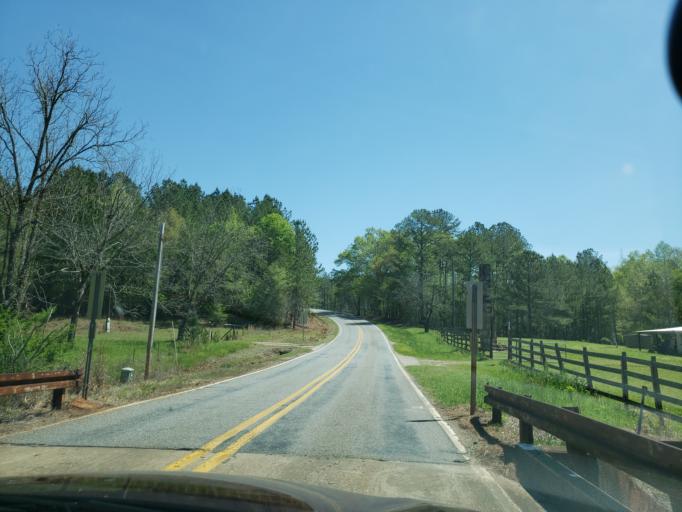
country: US
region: Alabama
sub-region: Elmore County
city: Tallassee
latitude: 32.6786
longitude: -85.8759
